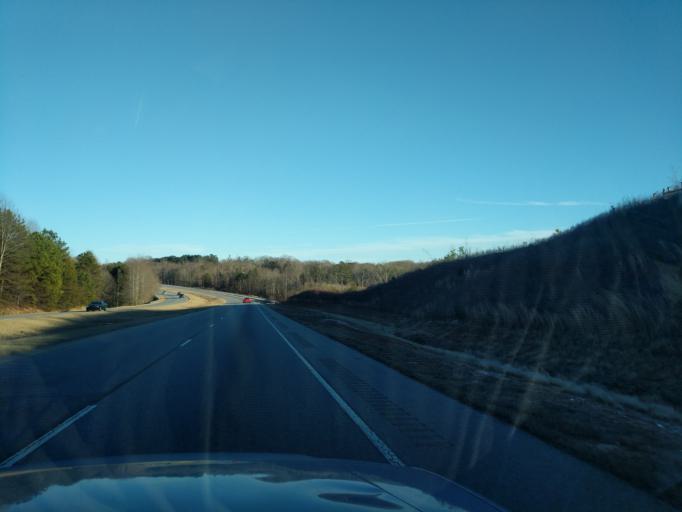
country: US
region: Georgia
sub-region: Stephens County
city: Toccoa
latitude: 34.5324
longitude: -83.3102
